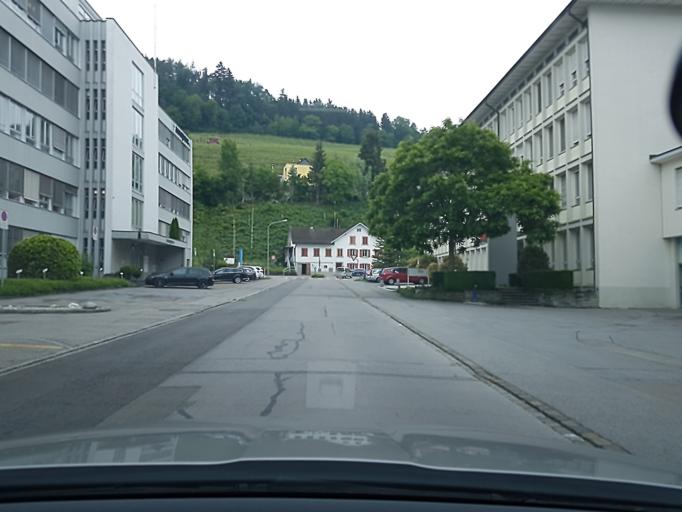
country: CH
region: Appenzell Innerrhoden
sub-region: Appenzell Inner Rhodes
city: Balgach
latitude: 47.4087
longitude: 9.6178
